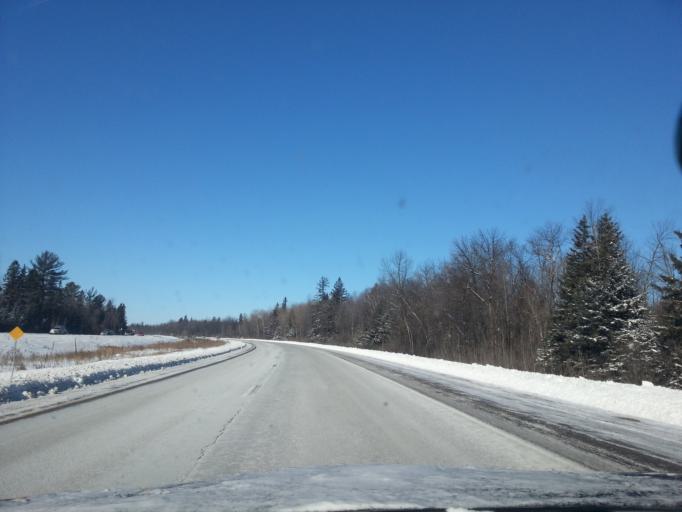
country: CA
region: Ontario
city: Carleton Place
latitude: 45.3084
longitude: -76.0386
